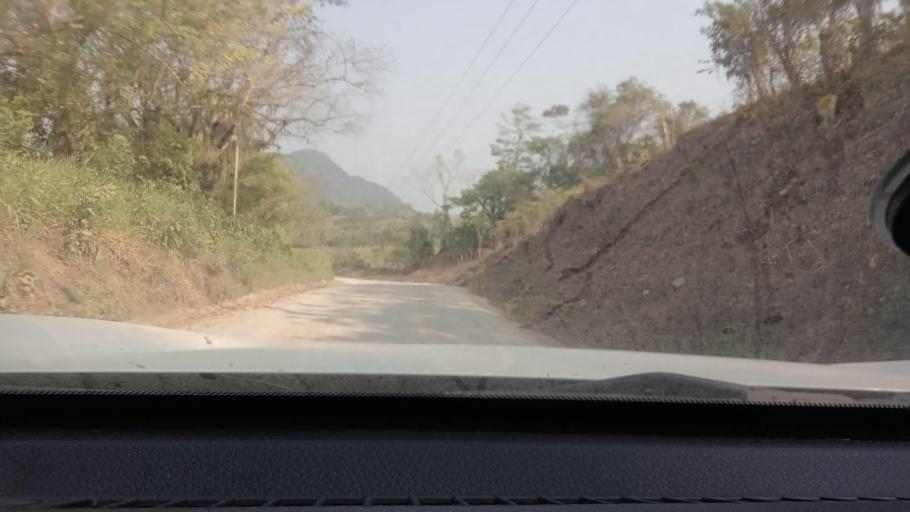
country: MX
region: Tabasco
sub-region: Huimanguillo
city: Francisco Rueda
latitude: 17.6129
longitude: -93.9376
